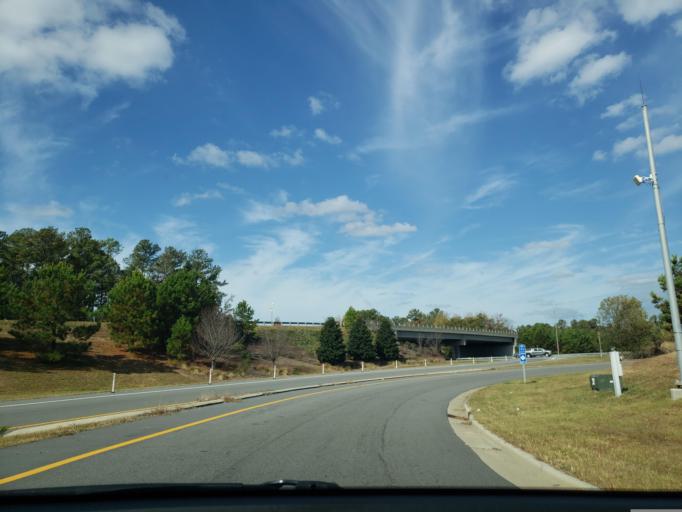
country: US
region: North Carolina
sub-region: Wake County
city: Green Level
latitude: 35.7456
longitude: -78.8936
